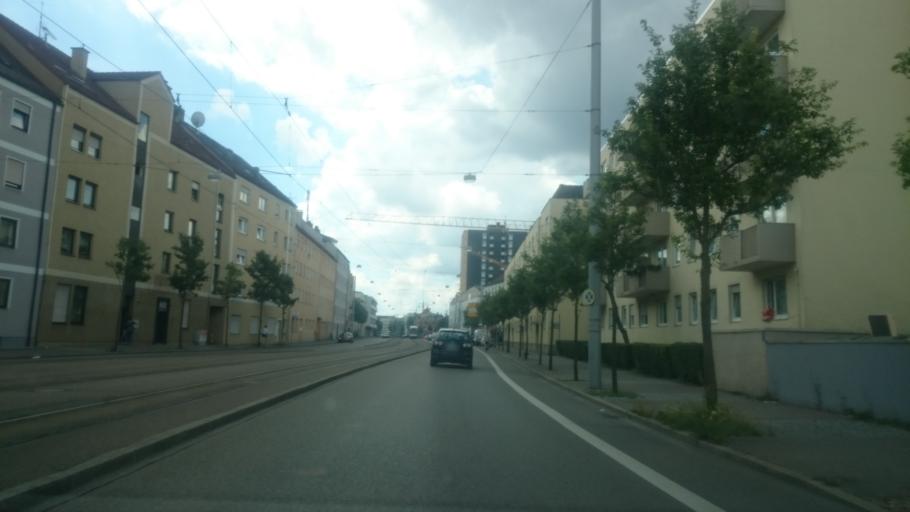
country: DE
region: Bavaria
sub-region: Swabia
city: Augsburg
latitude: 48.3882
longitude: 10.8813
